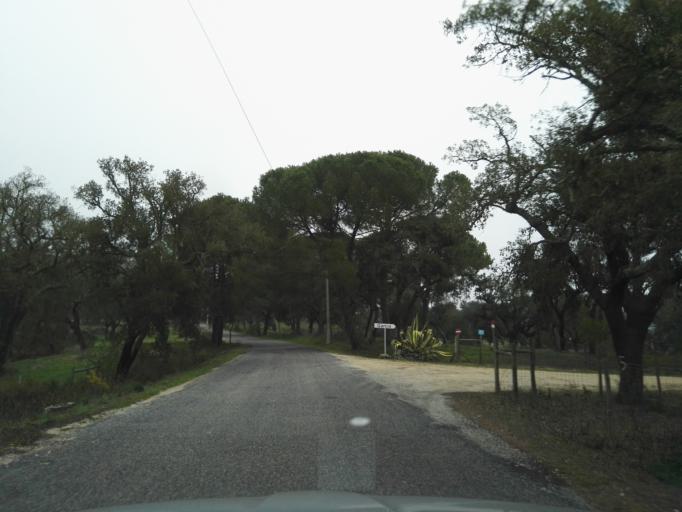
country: PT
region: Evora
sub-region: Vendas Novas
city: Vendas Novas
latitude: 38.7852
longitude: -8.3574
